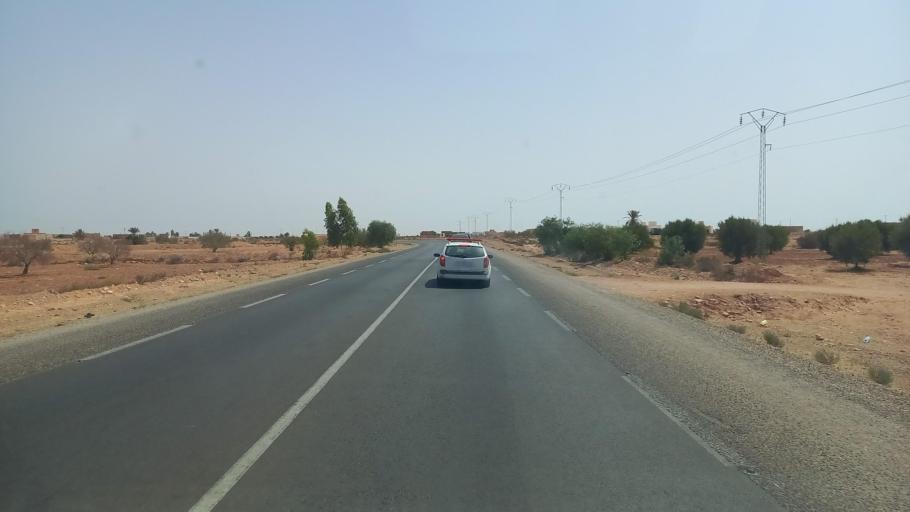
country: TN
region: Madanin
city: Medenine
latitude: 33.3695
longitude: 10.6836
